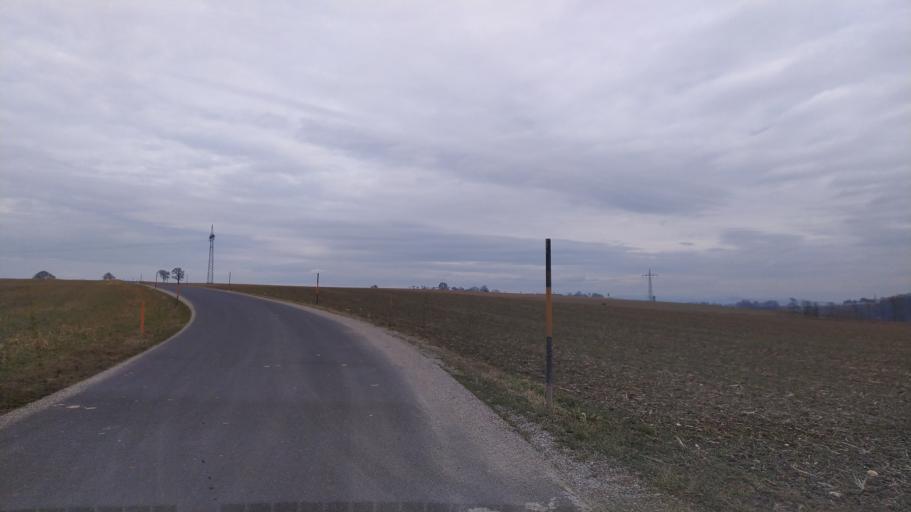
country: AT
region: Lower Austria
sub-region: Politischer Bezirk Amstetten
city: Strengberg
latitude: 48.1395
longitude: 14.7151
